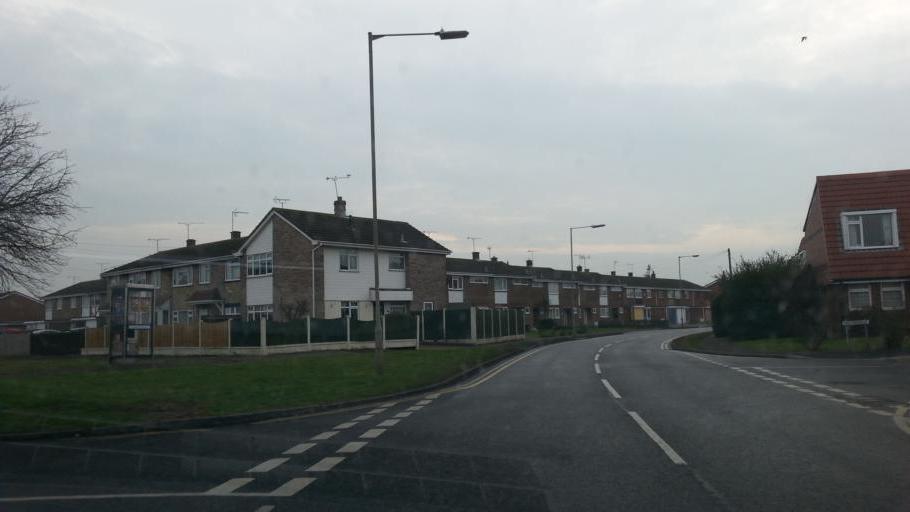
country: GB
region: England
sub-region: Essex
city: Canvey Island
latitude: 51.5274
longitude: 0.5743
